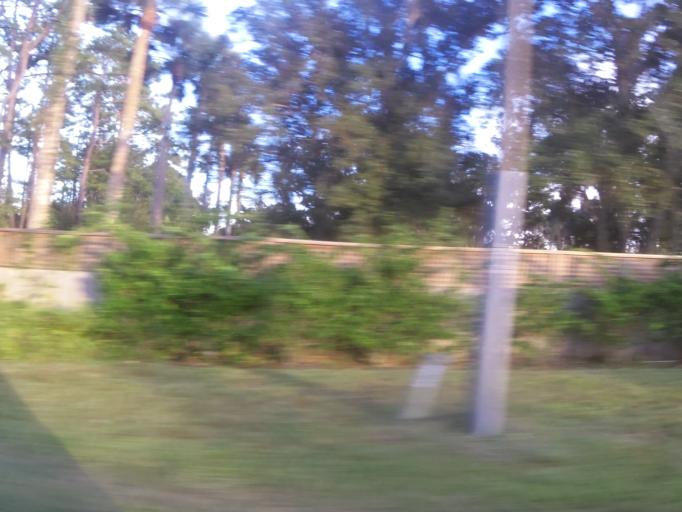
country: US
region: Florida
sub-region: Saint Johns County
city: Palm Valley
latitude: 30.1814
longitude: -81.3893
